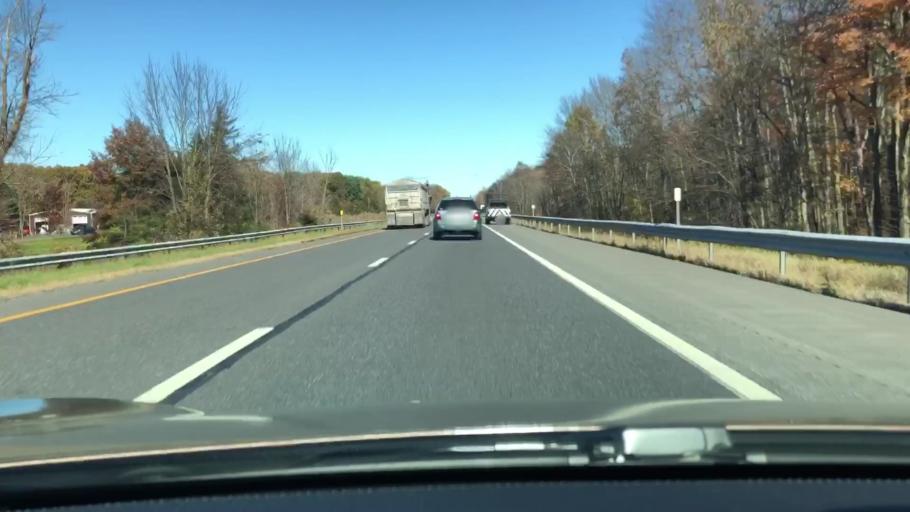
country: US
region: New York
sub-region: Ulster County
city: New Paltz
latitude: 41.7483
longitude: -74.0623
